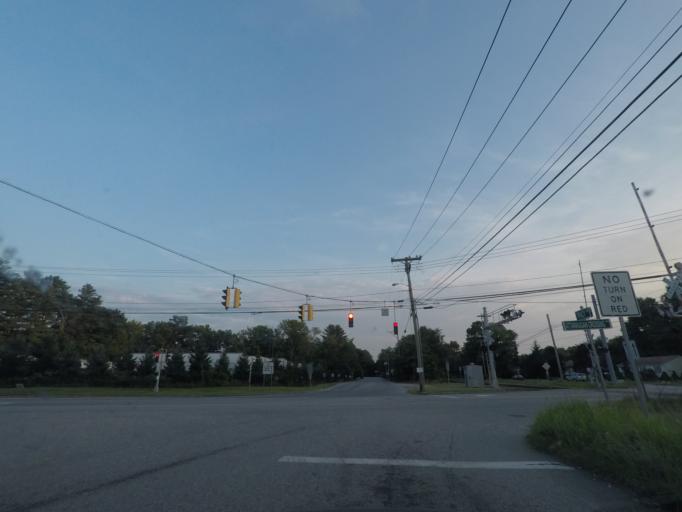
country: US
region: Connecticut
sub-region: Windham County
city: Killingly Center
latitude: 41.8674
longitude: -71.8933
